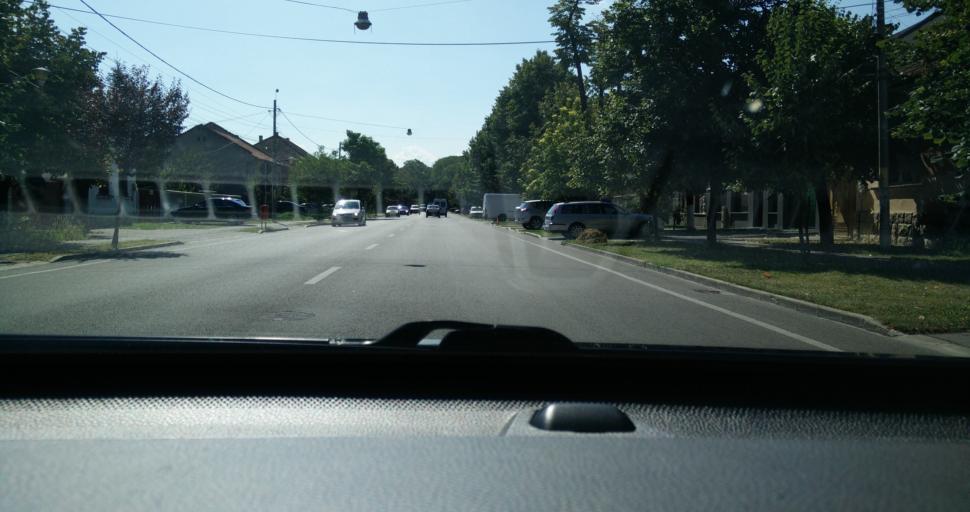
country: RO
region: Bihor
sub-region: Comuna Biharea
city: Oradea
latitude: 47.0463
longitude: 21.9321
